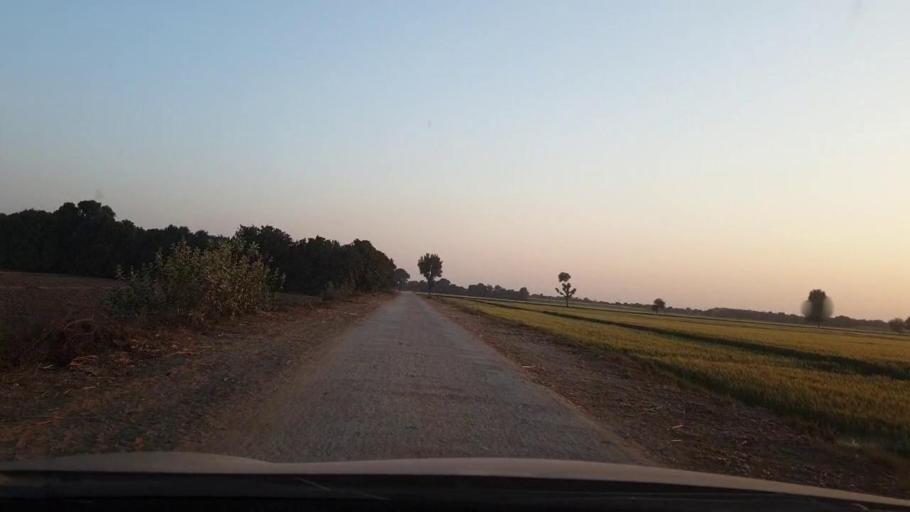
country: PK
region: Sindh
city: Tando Allahyar
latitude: 25.5204
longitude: 68.7461
